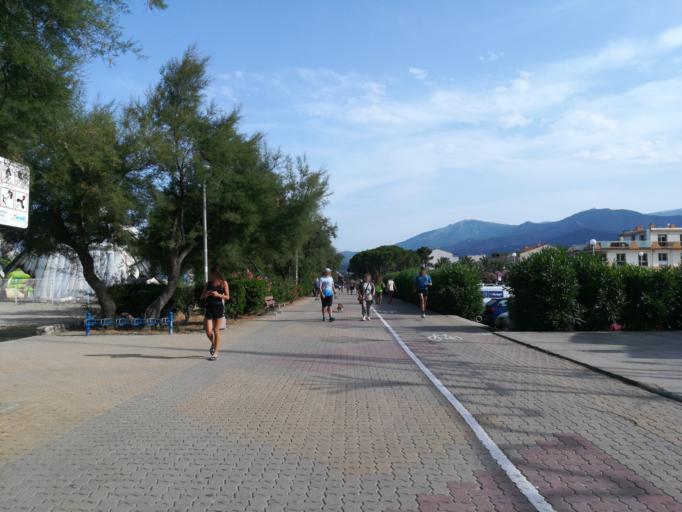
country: FR
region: Languedoc-Roussillon
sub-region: Departement des Pyrenees-Orientales
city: Argelers
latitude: 42.5543
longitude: 3.0477
